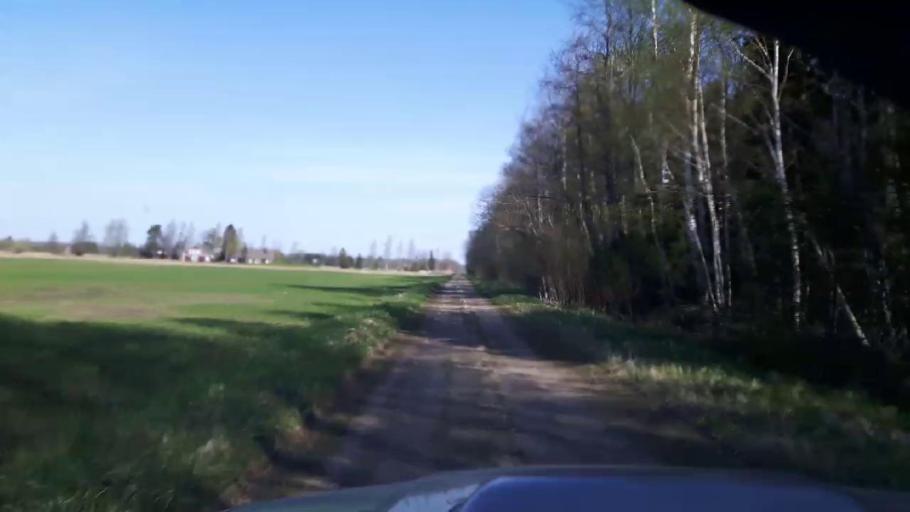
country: EE
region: Paernumaa
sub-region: Tootsi vald
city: Tootsi
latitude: 58.4776
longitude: 24.9257
